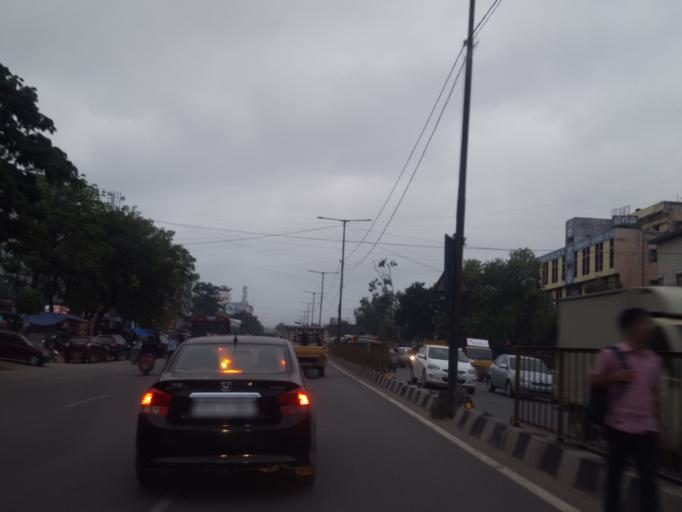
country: IN
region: Telangana
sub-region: Medak
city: Serilingampalle
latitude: 17.4951
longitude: 78.3231
